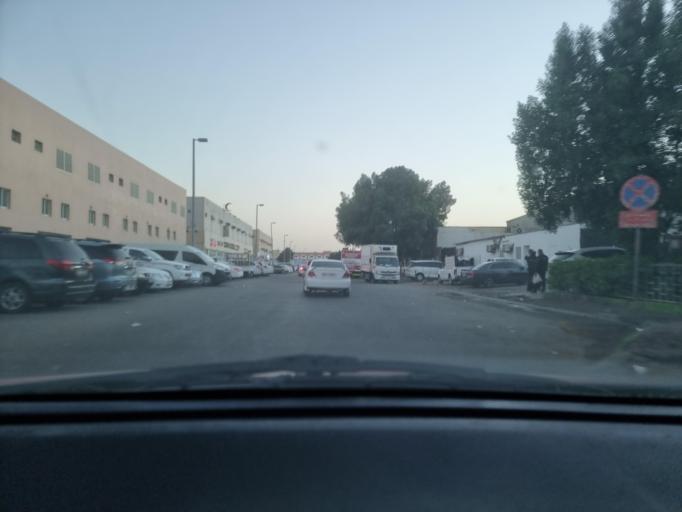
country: AE
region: Abu Dhabi
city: Abu Dhabi
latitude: 24.3514
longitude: 54.5204
